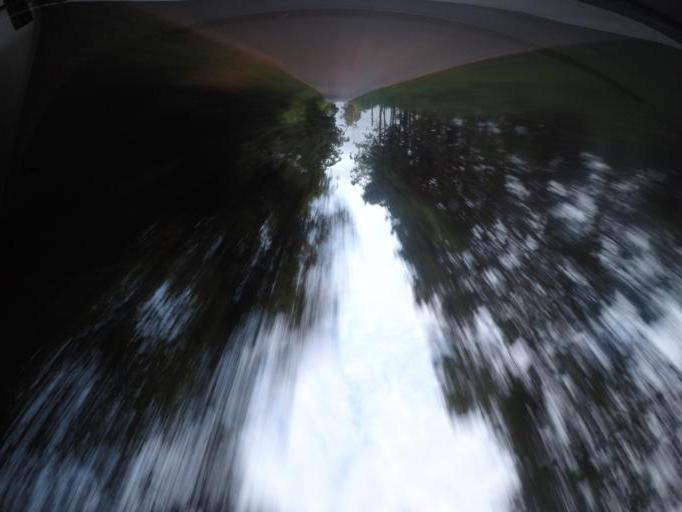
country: BR
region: Sao Paulo
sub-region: Aruja
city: Aruja
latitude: -23.3735
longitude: -46.2994
